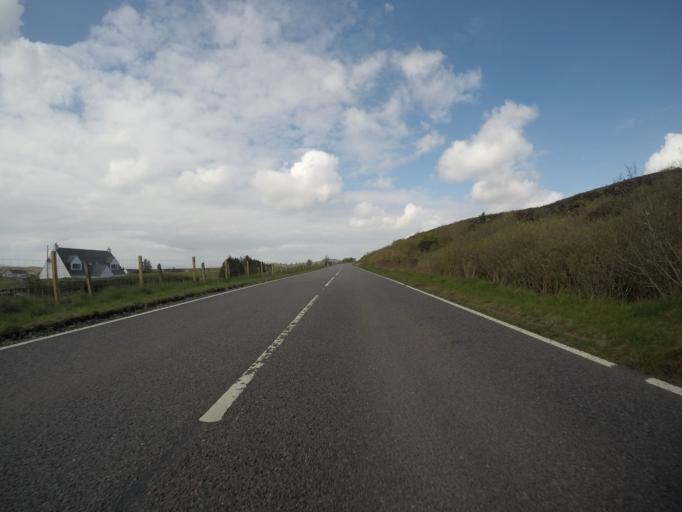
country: GB
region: Scotland
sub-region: Highland
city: Portree
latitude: 57.5609
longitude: -6.3637
